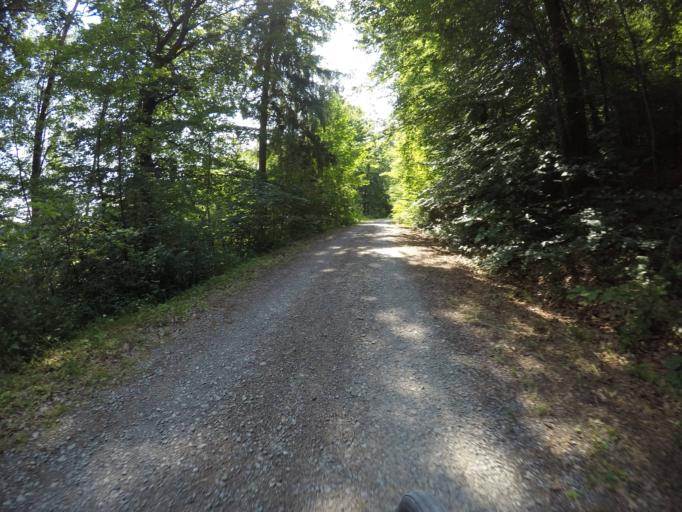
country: DE
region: Baden-Wuerttemberg
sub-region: Regierungsbezirk Stuttgart
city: Schlaitdorf
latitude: 48.6246
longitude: 9.1972
